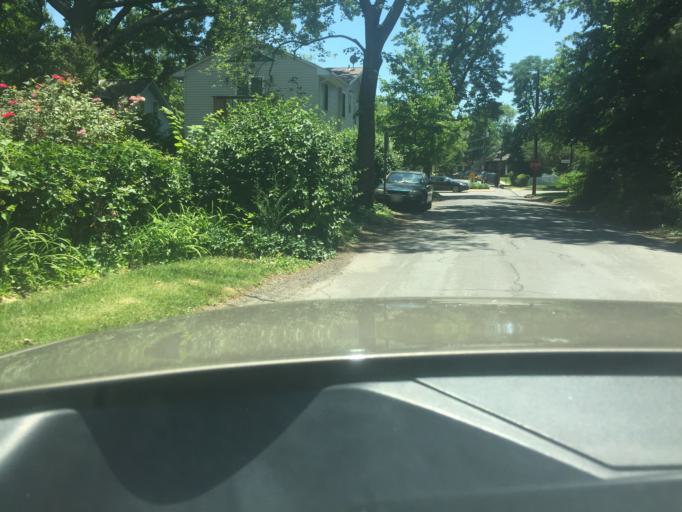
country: US
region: Virginia
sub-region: Arlington County
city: Arlington
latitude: 38.8931
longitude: -77.0910
